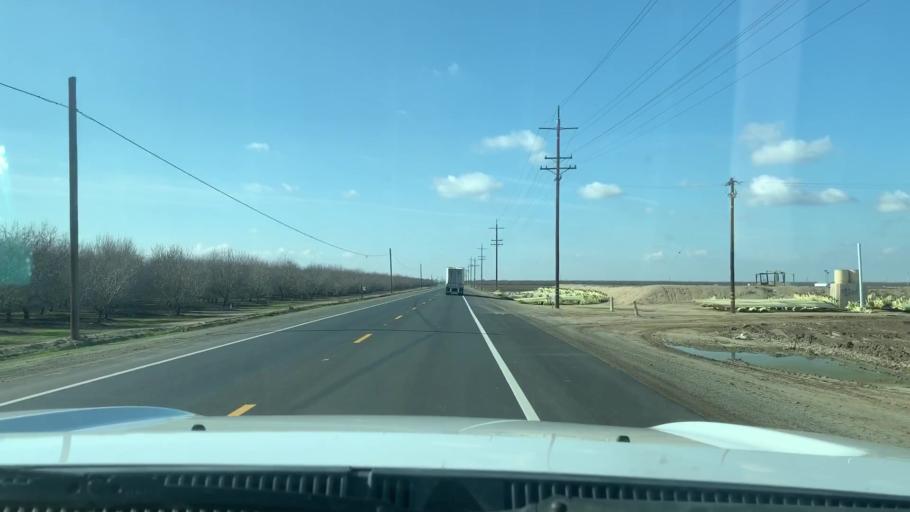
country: US
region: California
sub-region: Kern County
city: Wasco
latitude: 35.6017
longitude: -119.3031
